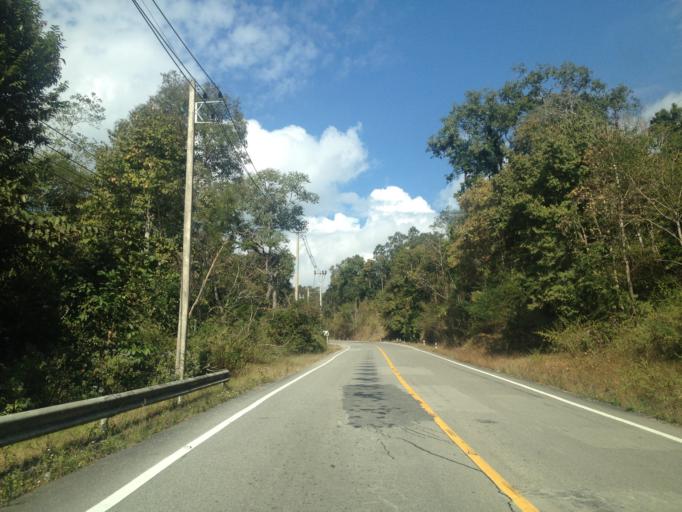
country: TH
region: Mae Hong Son
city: Ban Huai I Huak
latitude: 18.1389
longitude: 98.1735
